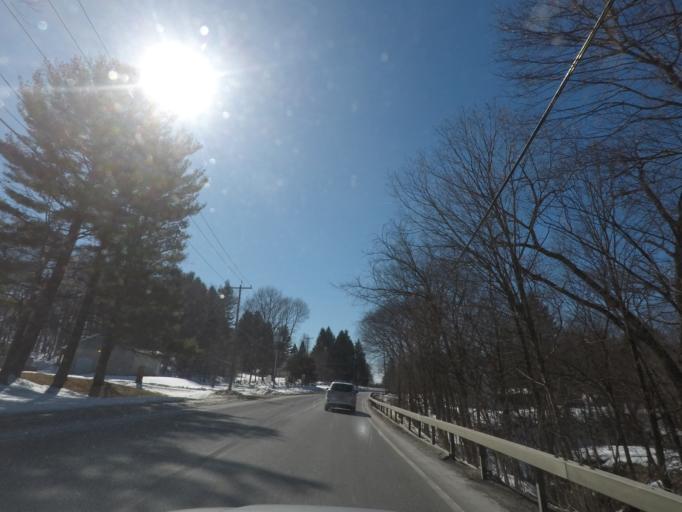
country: US
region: New York
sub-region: Saratoga County
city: Waterford
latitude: 42.7929
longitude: -73.6492
